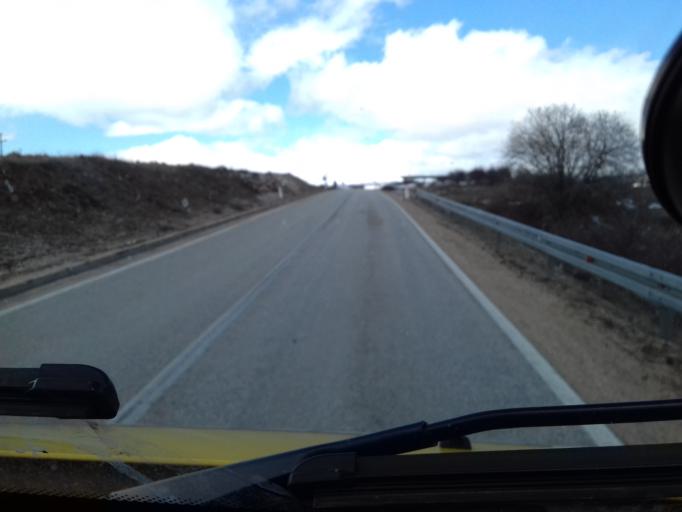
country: BA
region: Federation of Bosnia and Herzegovina
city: Tomislavgrad
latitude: 43.7667
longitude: 17.2372
